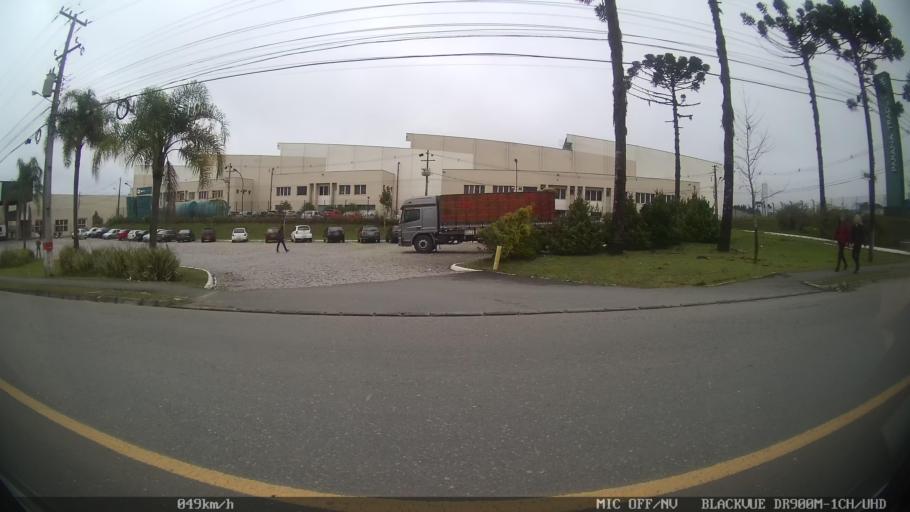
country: BR
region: Parana
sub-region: Sao Jose Dos Pinhais
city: Sao Jose dos Pinhais
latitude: -25.5698
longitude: -49.1726
